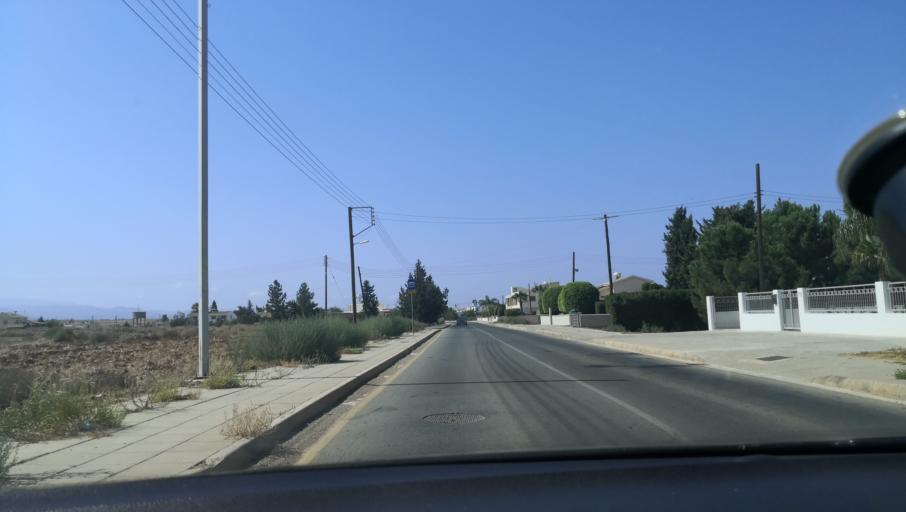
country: CY
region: Lefkosia
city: Kokkinotrimithia
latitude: 35.1148
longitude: 33.2177
